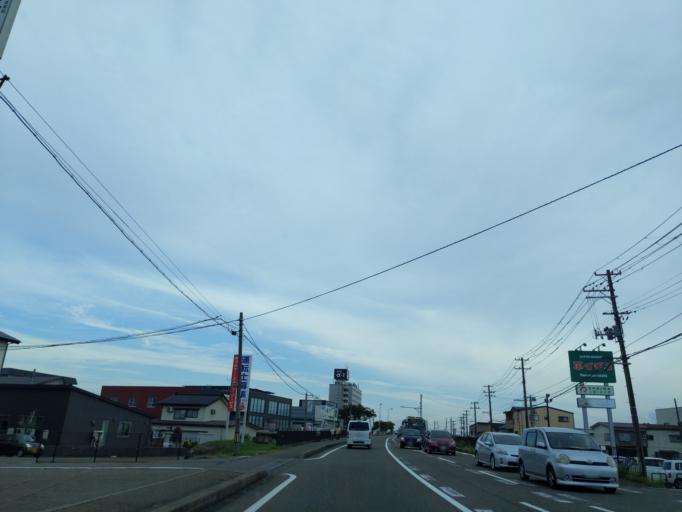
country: JP
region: Niigata
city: Joetsu
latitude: 37.1693
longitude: 138.2367
